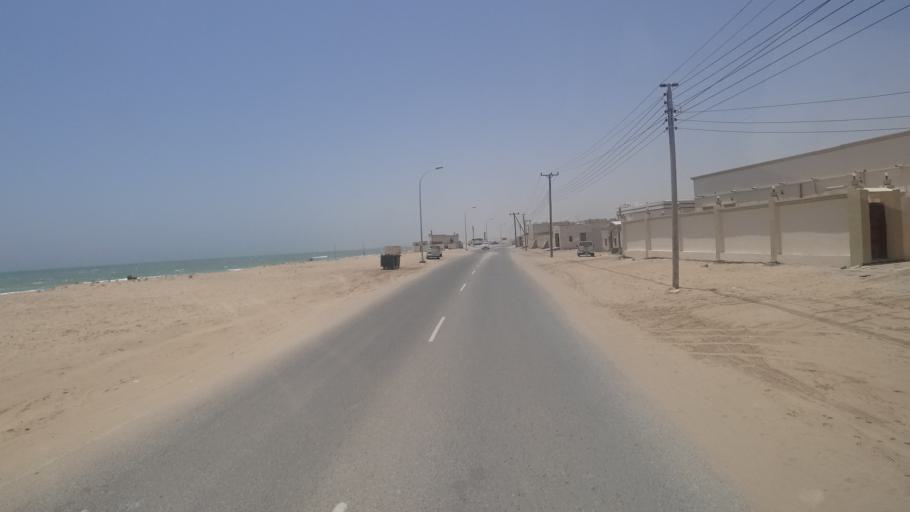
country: OM
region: Ash Sharqiyah
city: Sur
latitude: 22.0813
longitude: 59.6842
